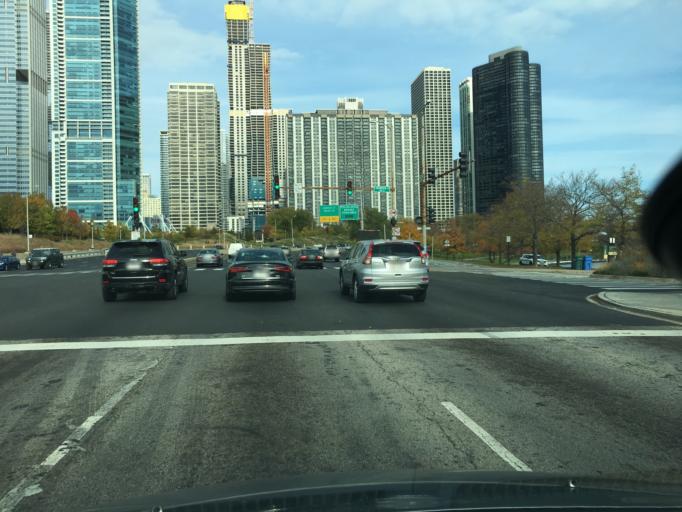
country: US
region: Illinois
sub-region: Cook County
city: Chicago
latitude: 41.8806
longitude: -87.6172
